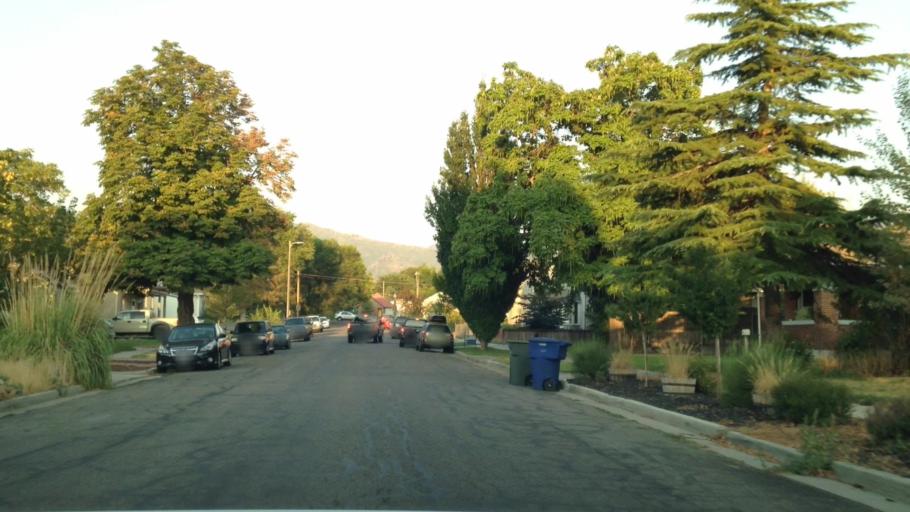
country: US
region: Utah
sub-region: Salt Lake County
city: South Salt Lake
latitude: 40.7276
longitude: -111.8734
